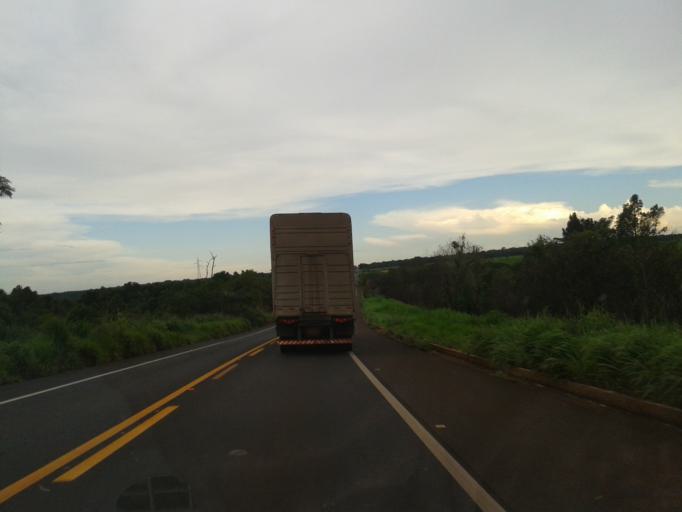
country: BR
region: Minas Gerais
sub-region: Santa Vitoria
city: Santa Vitoria
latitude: -18.9249
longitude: -50.2586
